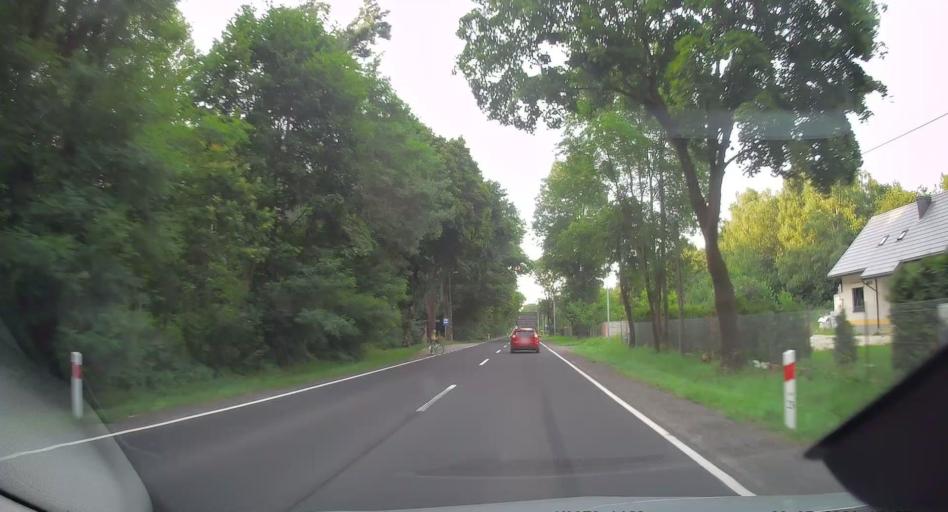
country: PL
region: Lodz Voivodeship
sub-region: Powiat radomszczanski
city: Gomunice
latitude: 51.1713
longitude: 19.4938
